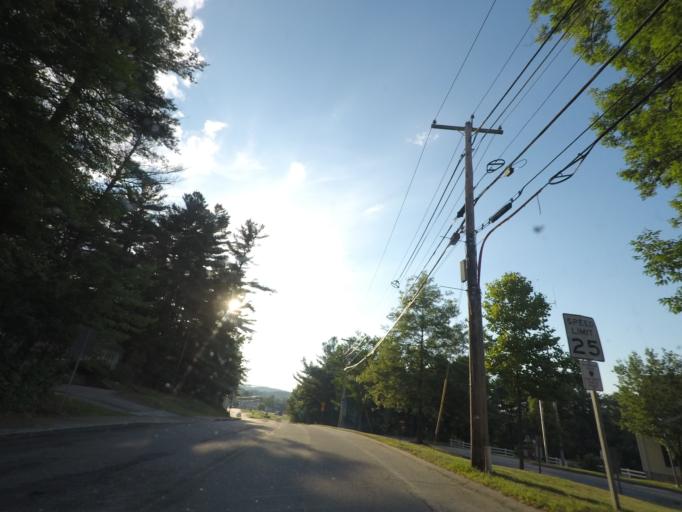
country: US
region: Massachusetts
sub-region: Worcester County
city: Sturbridge
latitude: 42.1110
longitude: -72.0844
